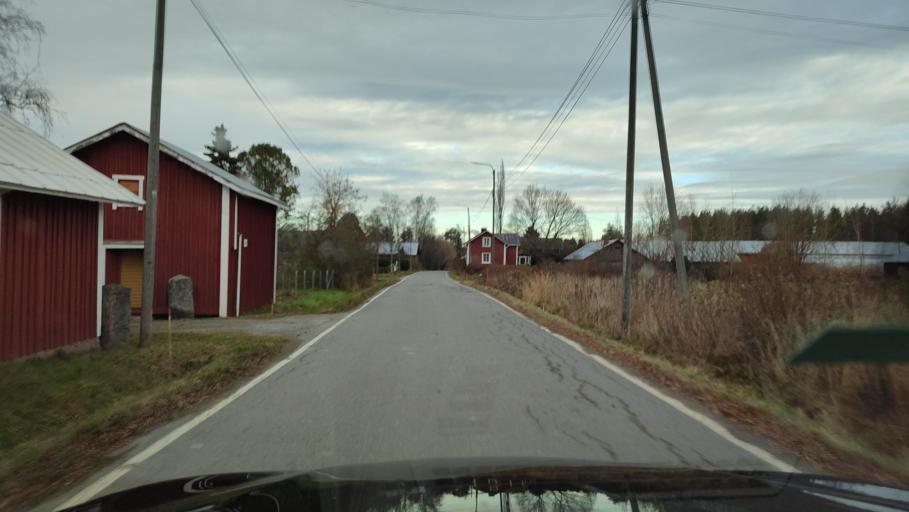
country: FI
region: Ostrobothnia
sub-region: Sydosterbotten
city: Naerpes
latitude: 62.4687
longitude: 21.3721
